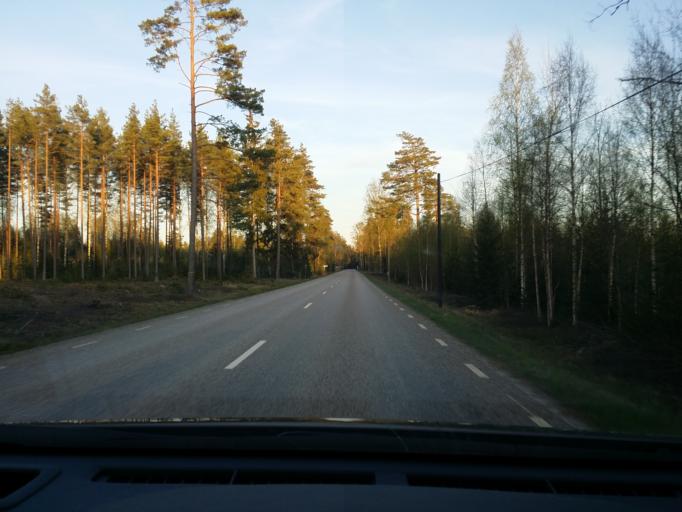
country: SE
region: Vaestmanland
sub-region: Sala Kommun
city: Sala
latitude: 59.8288
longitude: 16.5163
